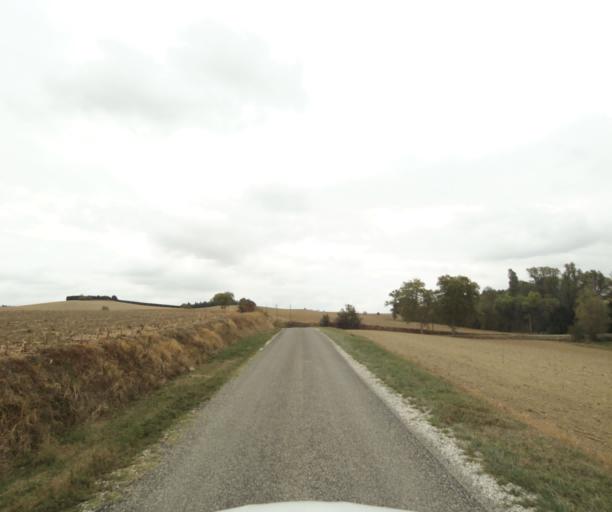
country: FR
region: Midi-Pyrenees
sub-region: Departement de la Haute-Garonne
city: Villefranche-de-Lauragais
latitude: 43.4029
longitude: 1.7342
